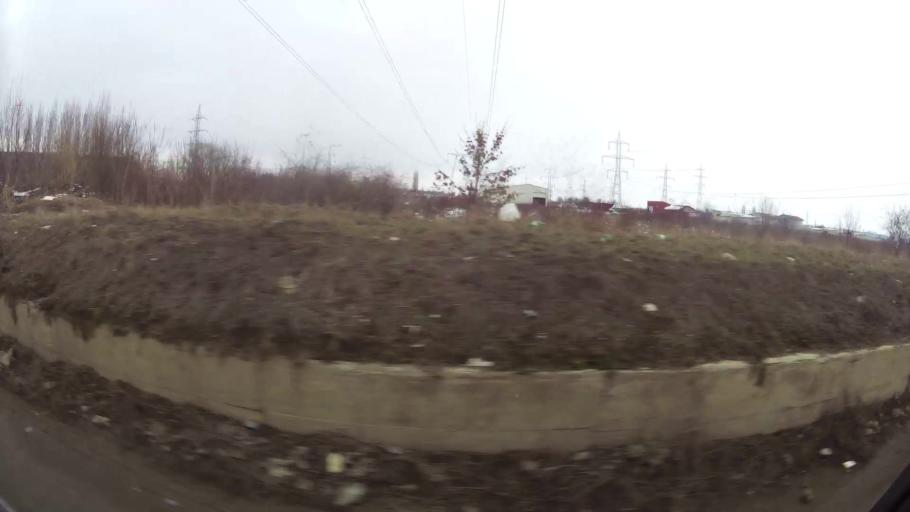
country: RO
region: Ilfov
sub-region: Comuna Glina
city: Catelu
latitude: 44.3977
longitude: 26.2019
